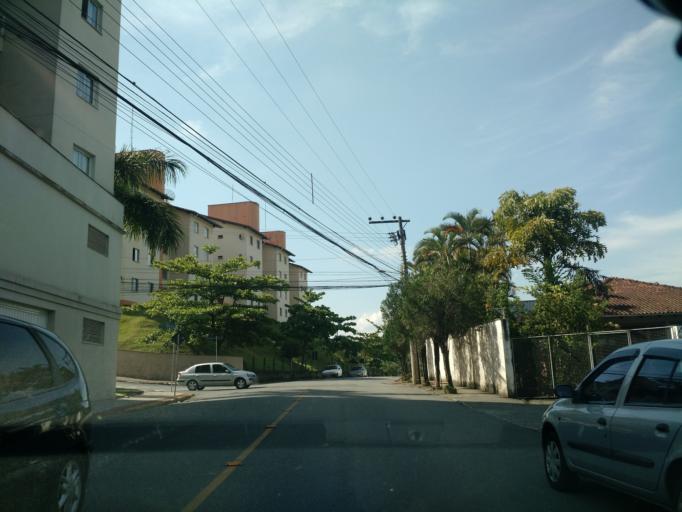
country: BR
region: Santa Catarina
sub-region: Jaragua Do Sul
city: Jaragua do Sul
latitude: -26.5011
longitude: -49.0971
